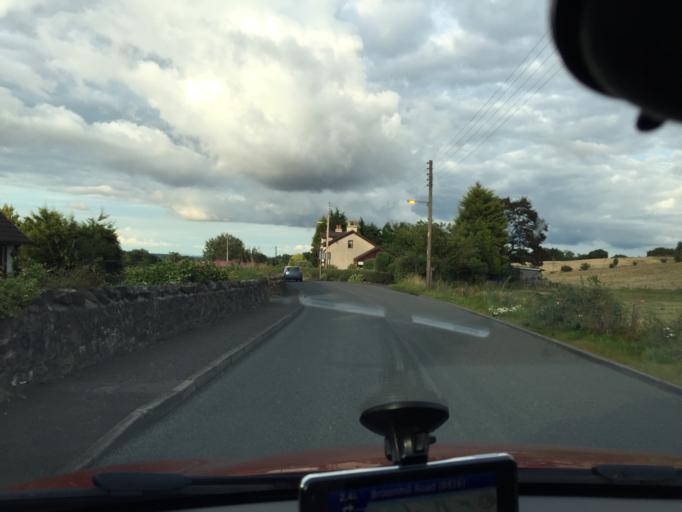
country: GB
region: Scotland
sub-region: Falkirk
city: Bonnybridge
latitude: 55.9874
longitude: -3.9192
